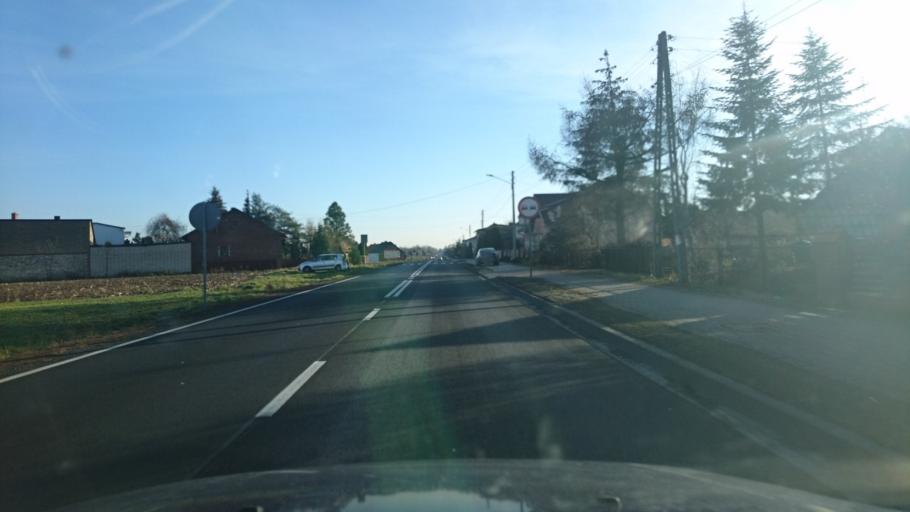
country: PL
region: Silesian Voivodeship
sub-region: Powiat klobucki
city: Starokrzepice
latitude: 51.0018
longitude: 18.6642
